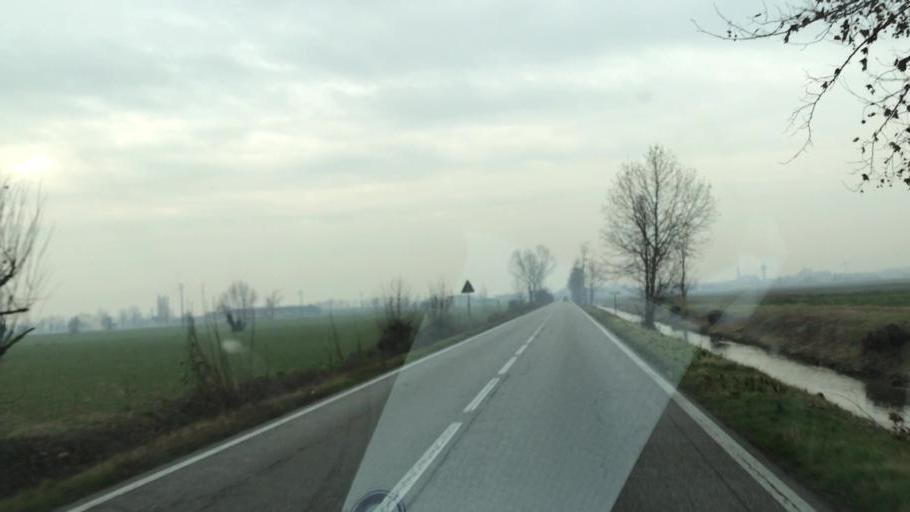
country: IT
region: Lombardy
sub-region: Provincia di Mantova
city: Asola
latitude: 45.2396
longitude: 10.4161
